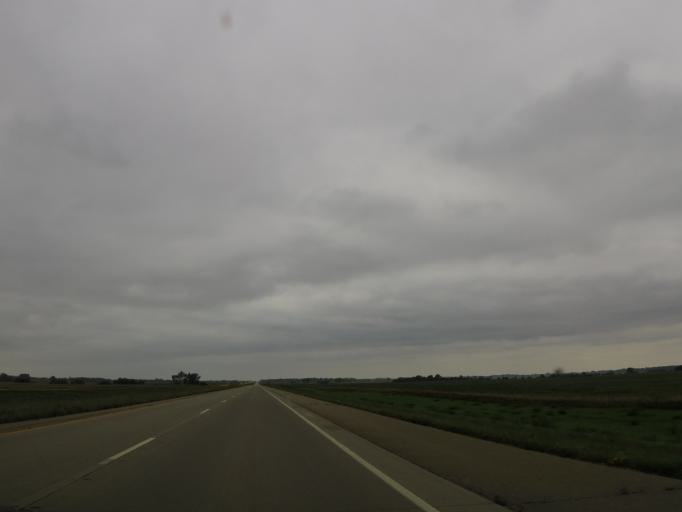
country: US
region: South Dakota
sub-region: Roberts County
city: Sisseton
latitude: 45.5546
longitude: -96.9892
